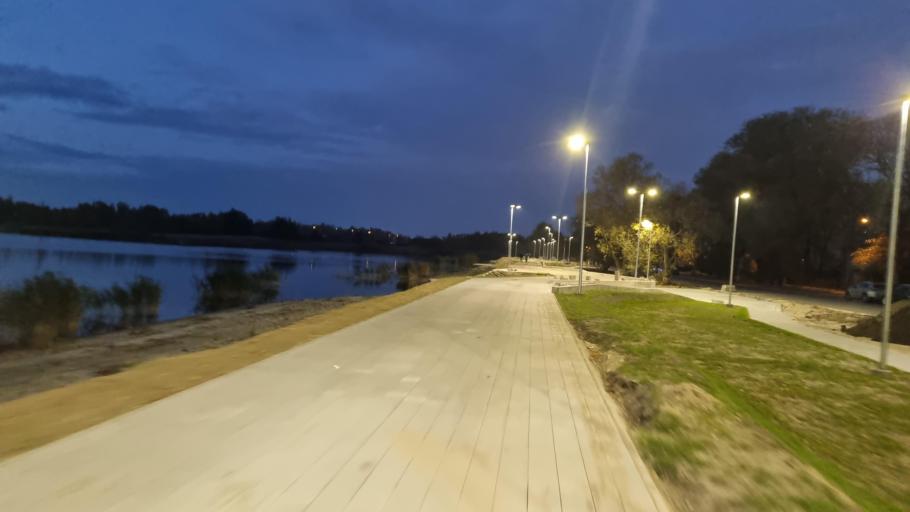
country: LV
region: Riga
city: Daugavgriva
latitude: 57.0318
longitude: 24.0339
